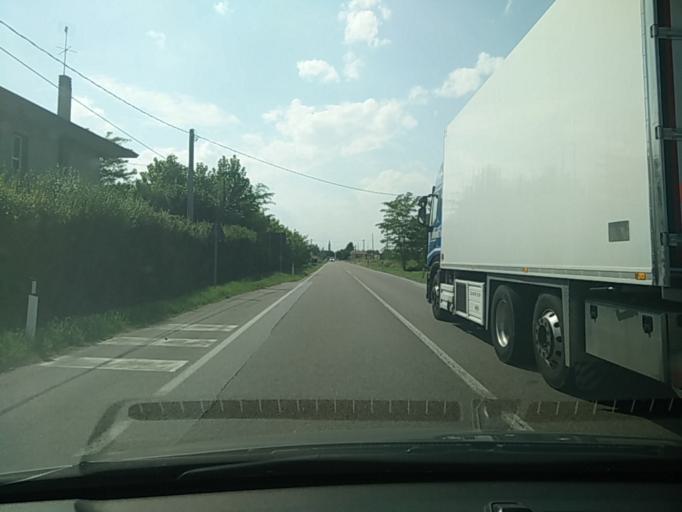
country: IT
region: Veneto
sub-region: Provincia di Treviso
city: Fanzolo
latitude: 45.6967
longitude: 11.9869
